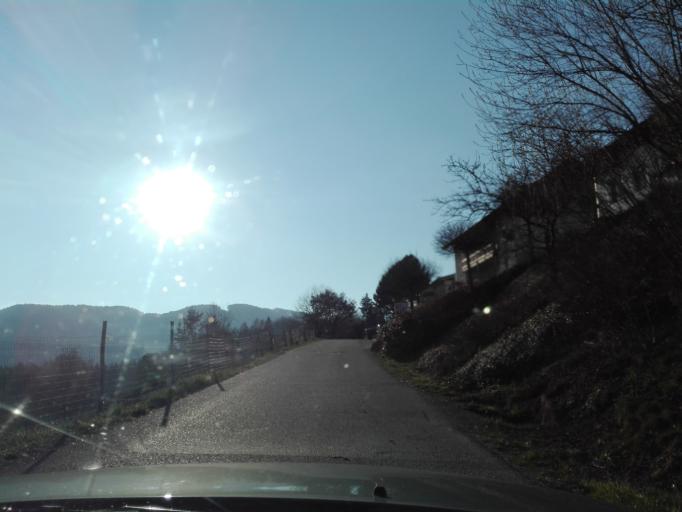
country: AT
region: Upper Austria
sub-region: Politischer Bezirk Rohrbach
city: Kleinzell im Muehlkreis
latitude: 48.3765
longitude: 13.9713
